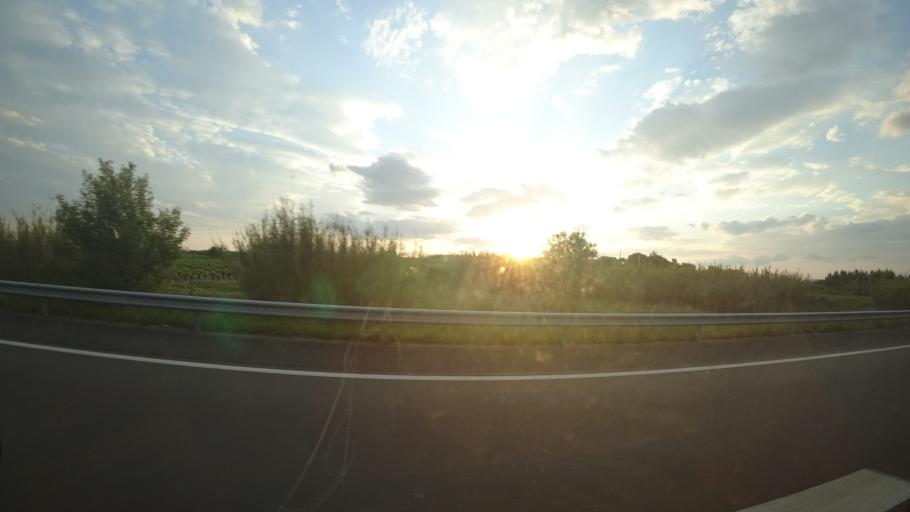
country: FR
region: Languedoc-Roussillon
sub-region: Departement de l'Herault
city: Paulhan
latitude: 43.5215
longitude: 3.4433
